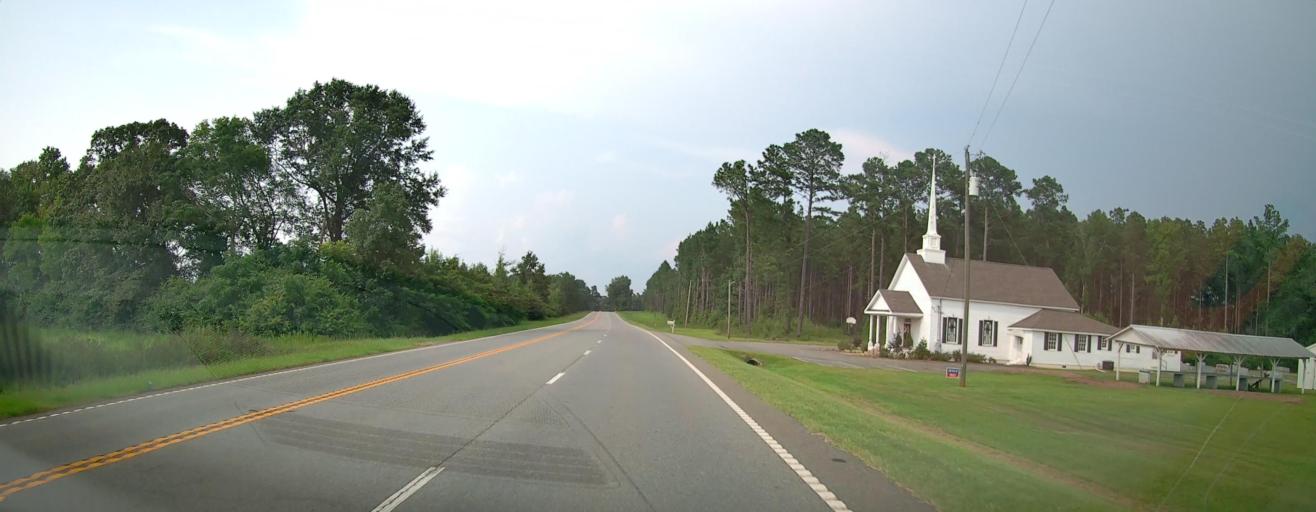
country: US
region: Georgia
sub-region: Twiggs County
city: Jeffersonville
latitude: 32.5682
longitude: -83.4089
